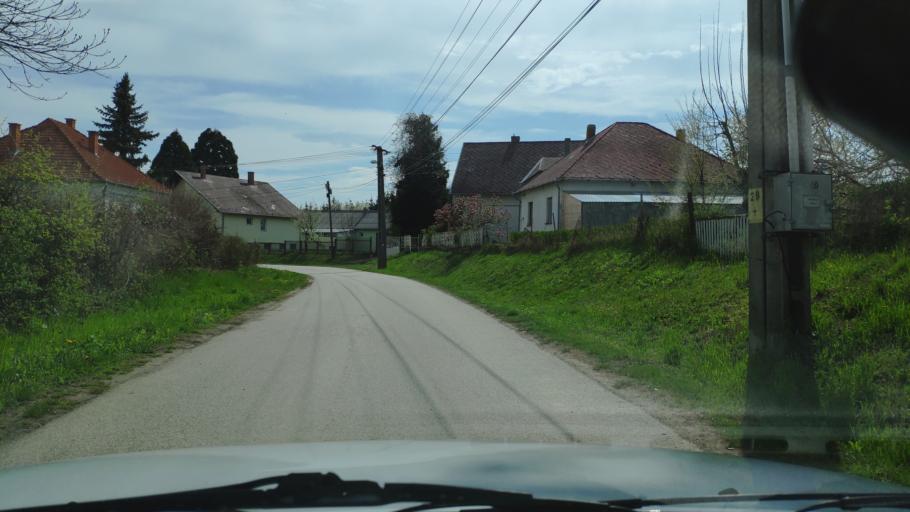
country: HU
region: Zala
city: Nagykanizsa
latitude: 46.4258
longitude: 17.0228
